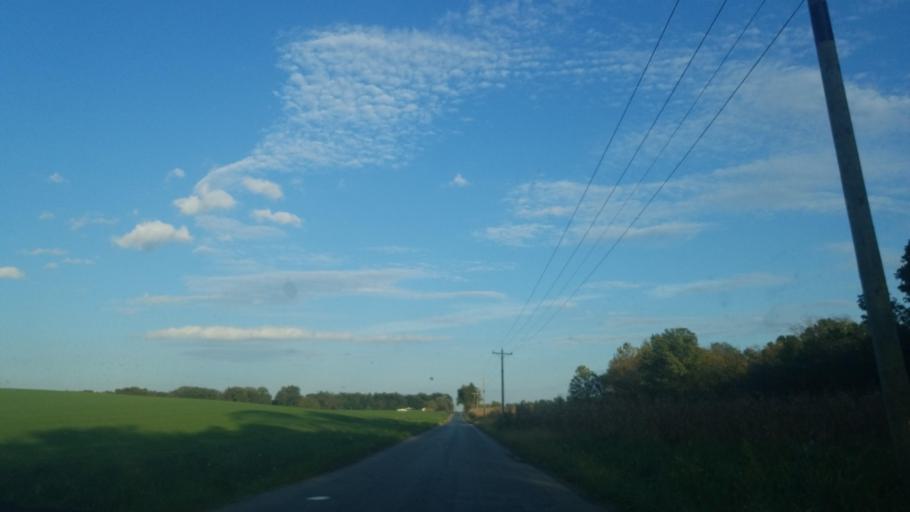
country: US
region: Illinois
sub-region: Saline County
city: Harrisburg
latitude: 37.8049
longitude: -88.6334
